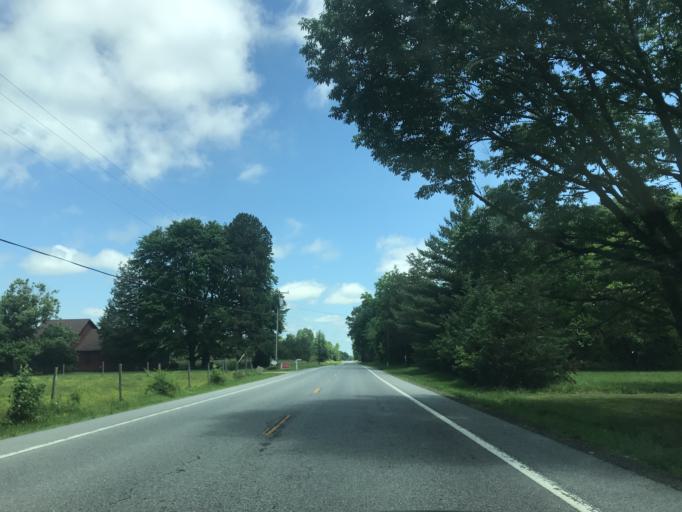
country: US
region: Maryland
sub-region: Caroline County
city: Federalsburg
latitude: 38.7112
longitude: -75.7460
